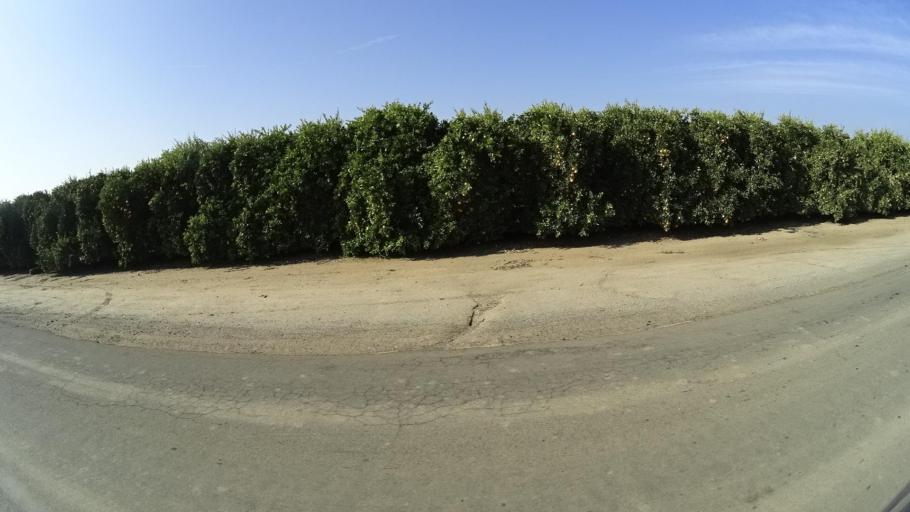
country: US
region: California
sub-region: Kern County
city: McFarland
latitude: 35.6675
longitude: -119.1692
